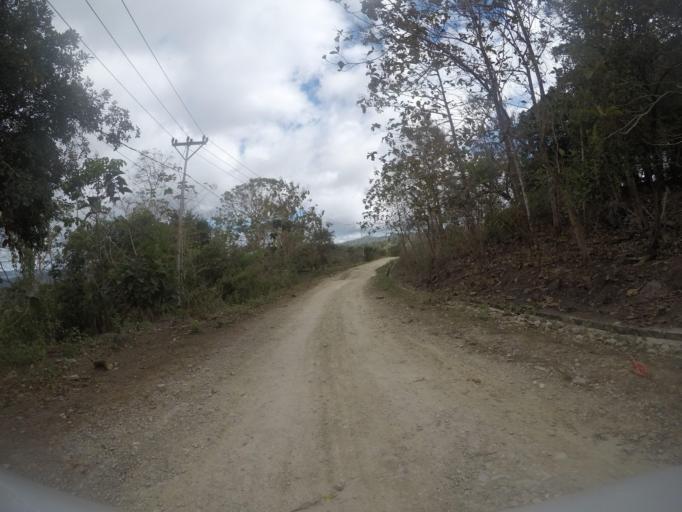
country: TL
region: Lautem
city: Lospalos
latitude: -8.5594
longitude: 126.8960
